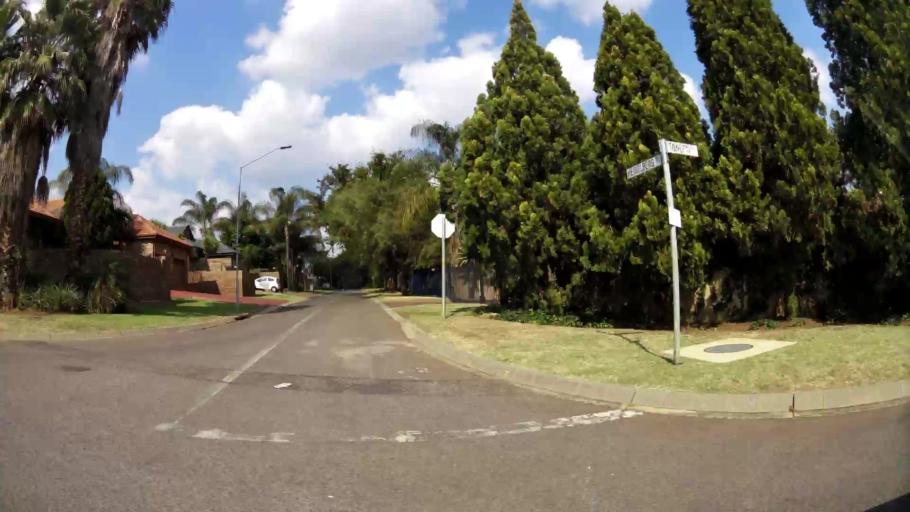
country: ZA
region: Gauteng
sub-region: City of Tshwane Metropolitan Municipality
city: Pretoria
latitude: -25.7947
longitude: 28.3280
